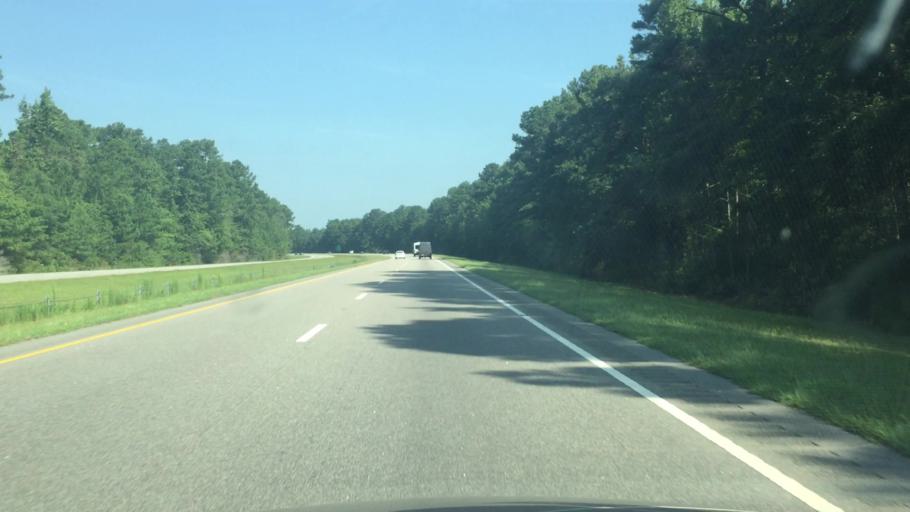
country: US
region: North Carolina
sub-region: Robeson County
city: Lumberton
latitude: 34.5627
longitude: -79.0274
